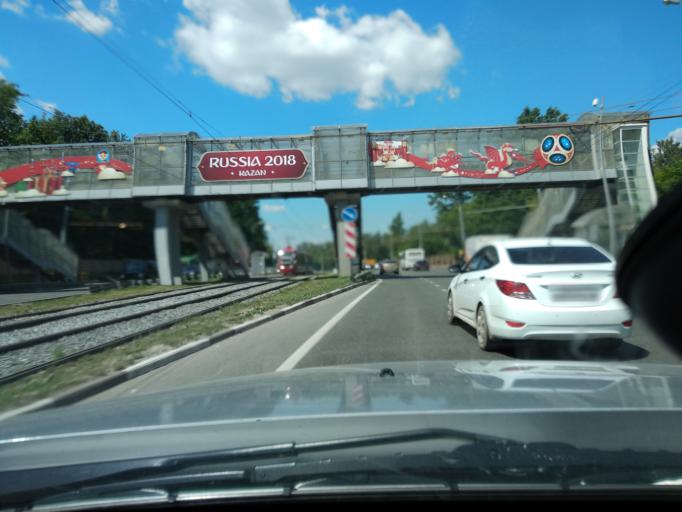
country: RU
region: Tatarstan
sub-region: Gorod Kazan'
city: Kazan
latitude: 55.8184
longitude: 49.1776
